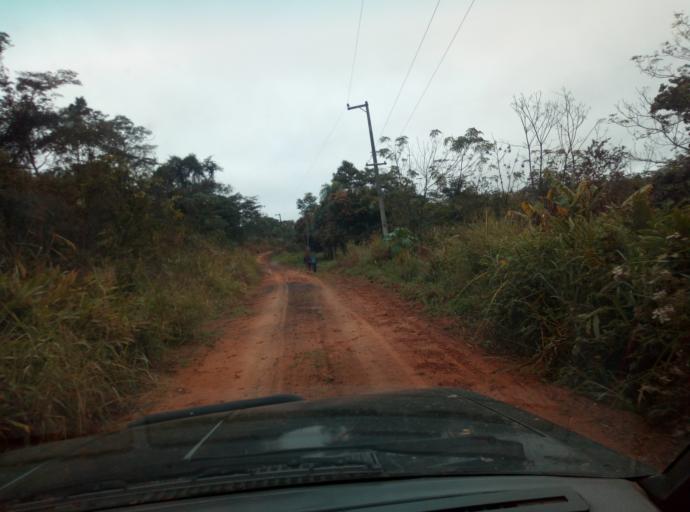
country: PY
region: Caaguazu
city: Carayao
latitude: -25.1904
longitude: -56.3598
